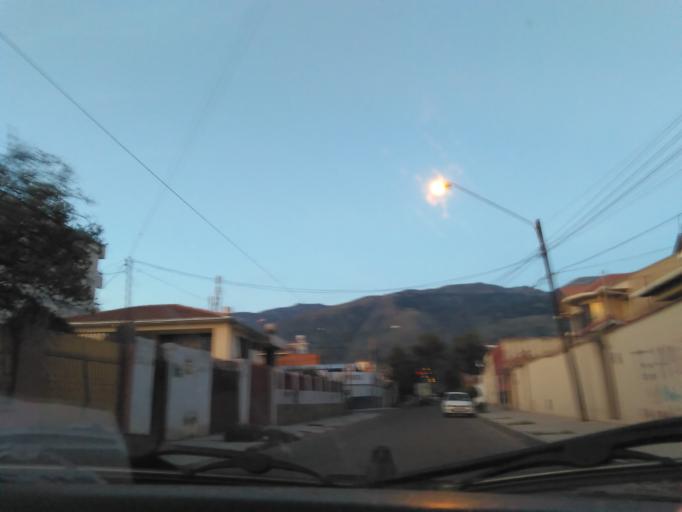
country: BO
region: Cochabamba
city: Cochabamba
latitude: -17.3735
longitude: -66.1661
